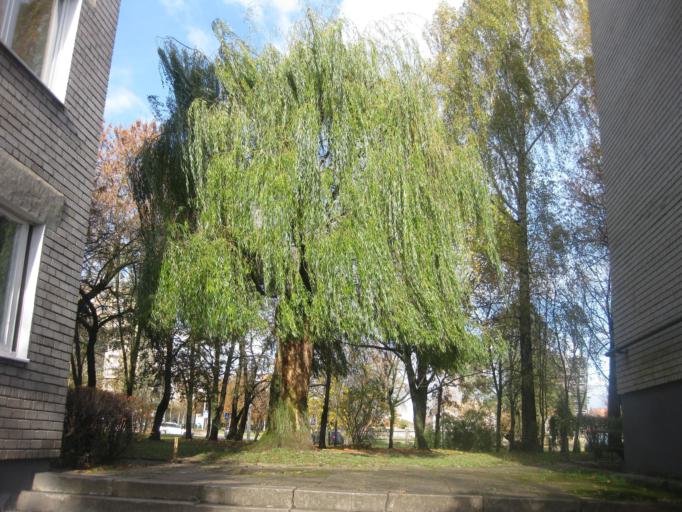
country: LT
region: Kauno apskritis
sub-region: Kaunas
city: Eiguliai
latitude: 54.9071
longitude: 23.9419
